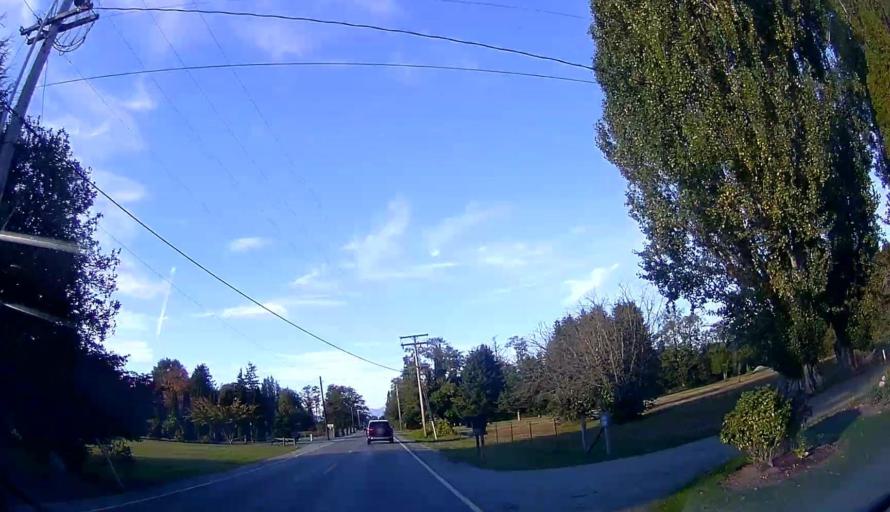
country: US
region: Washington
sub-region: Skagit County
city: Burlington
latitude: 48.4579
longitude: -122.3571
